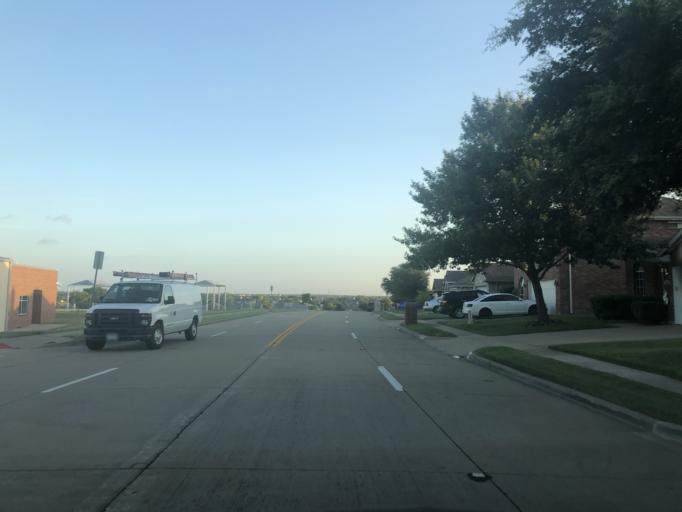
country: US
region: Texas
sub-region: Dallas County
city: Duncanville
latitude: 32.6527
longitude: -96.9729
